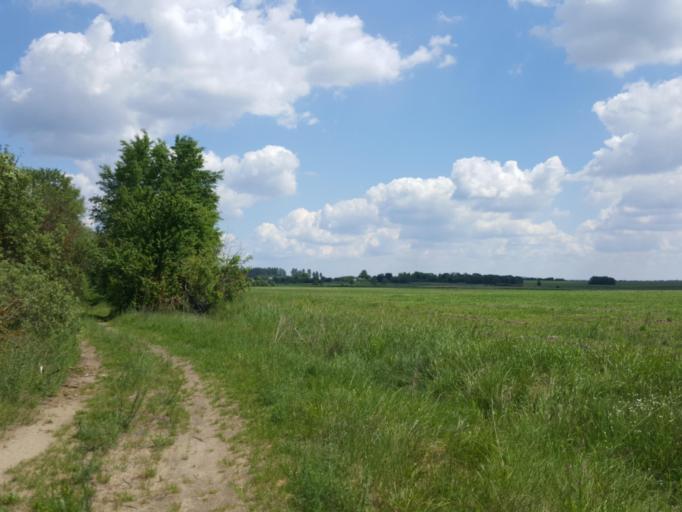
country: BY
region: Brest
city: Kamyanyets
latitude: 52.4380
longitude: 23.7198
